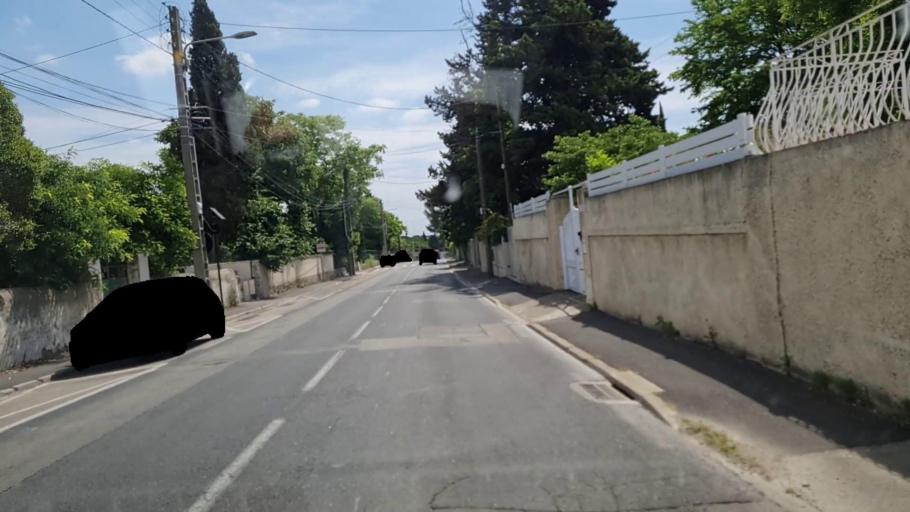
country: FR
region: Languedoc-Roussillon
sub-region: Departement du Gard
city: Nimes
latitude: 43.8377
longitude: 4.3264
